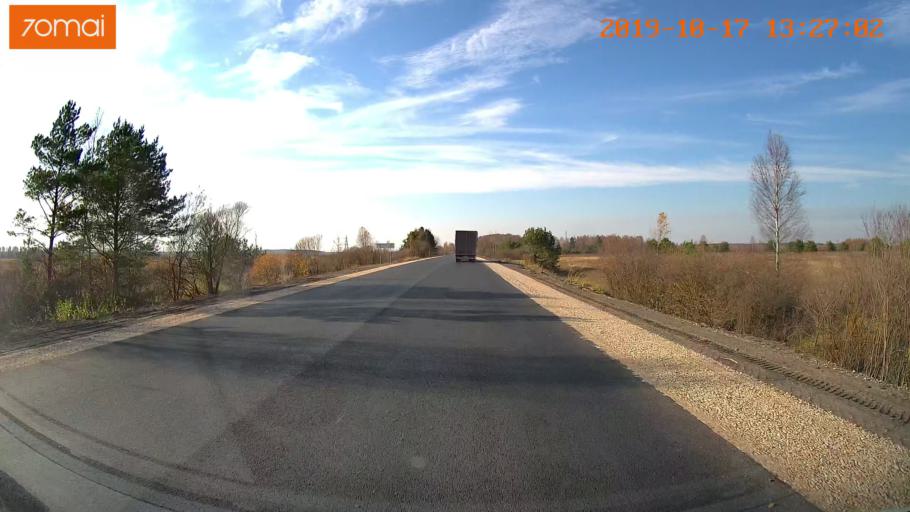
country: RU
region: Rjazan
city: Gus'-Zheleznyy
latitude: 55.1119
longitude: 40.9048
